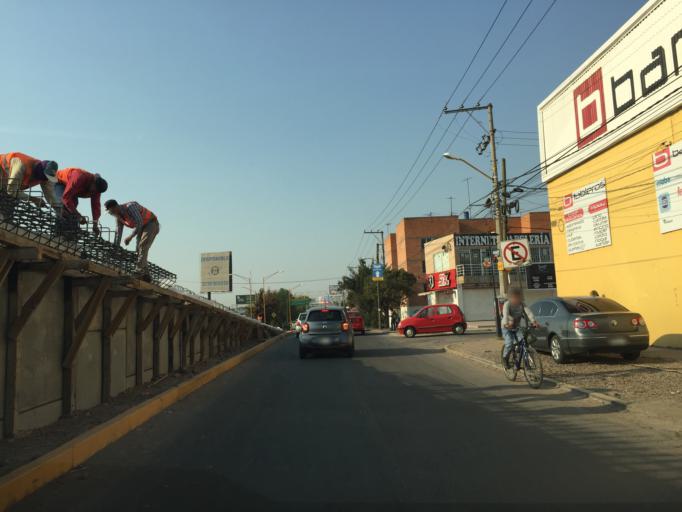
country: MX
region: Aguascalientes
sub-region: Aguascalientes
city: La Loma de los Negritos
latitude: 21.8706
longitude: -102.3186
